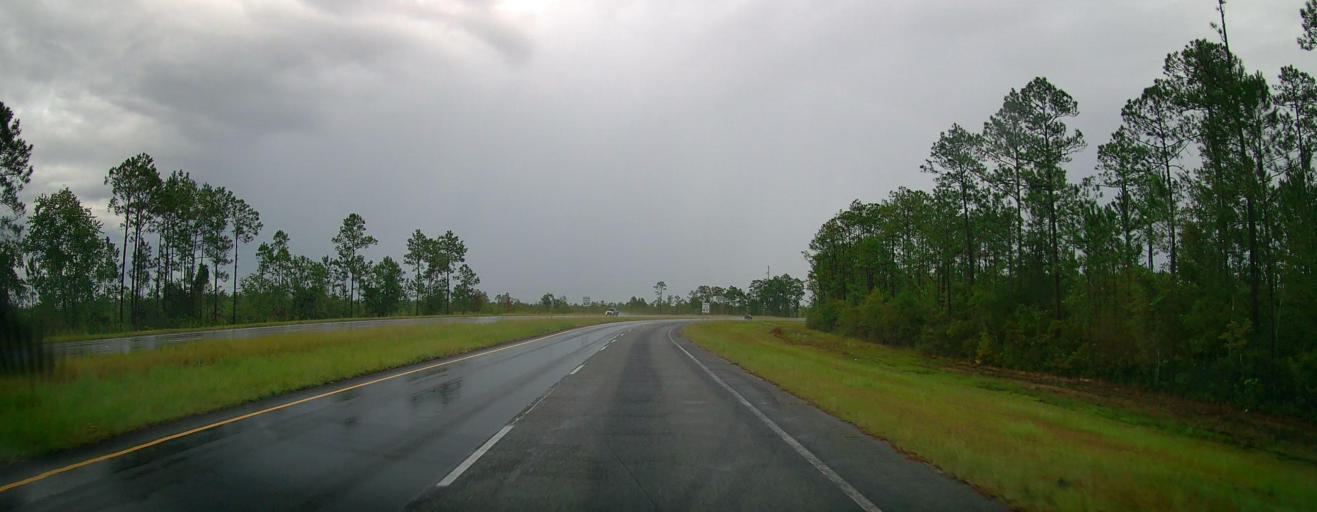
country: US
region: Georgia
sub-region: Ware County
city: Deenwood
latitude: 31.2491
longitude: -82.4406
